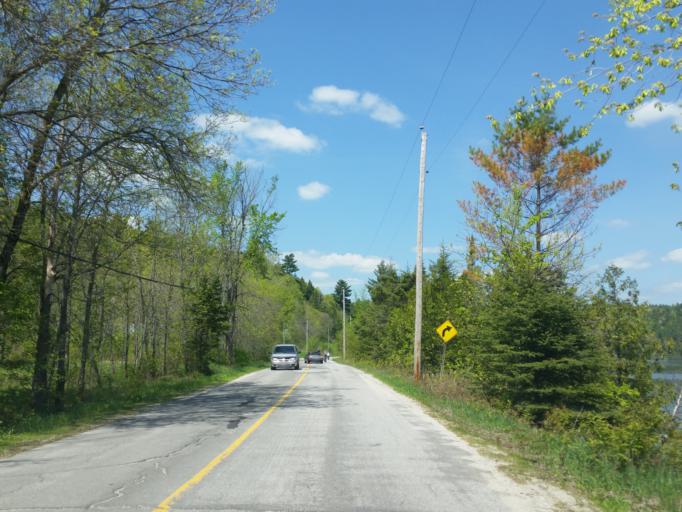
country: CA
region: Quebec
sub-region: Outaouais
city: Wakefield
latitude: 45.6226
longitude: -75.9030
